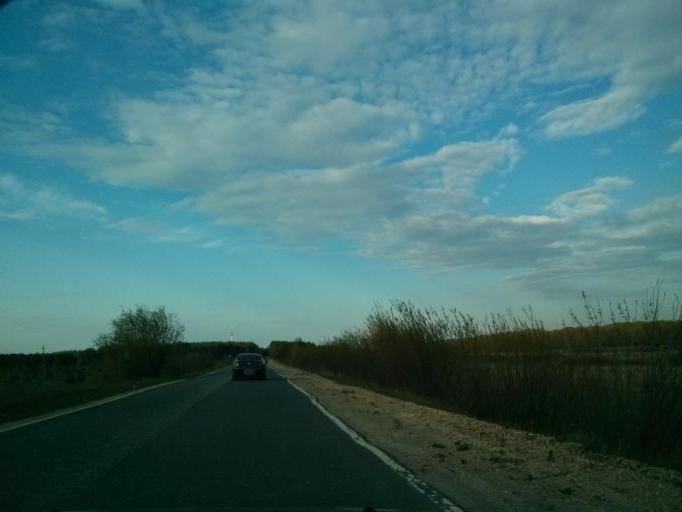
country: RU
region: Nizjnij Novgorod
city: Navashino
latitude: 55.5935
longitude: 42.1541
